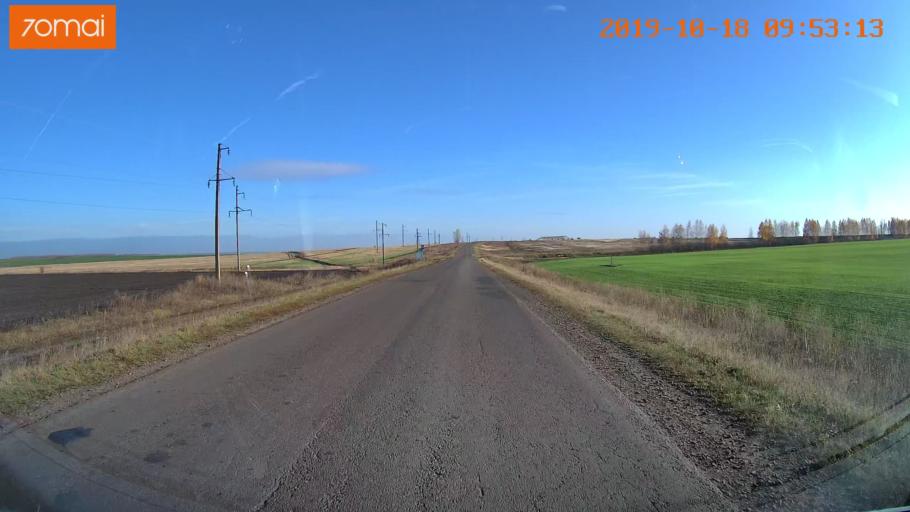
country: RU
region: Tula
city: Kazachka
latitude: 53.3589
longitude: 38.3238
